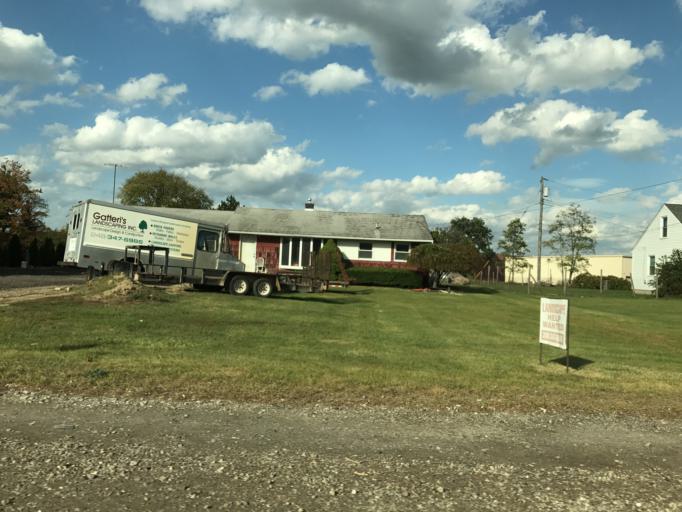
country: US
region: Michigan
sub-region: Oakland County
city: Wixom
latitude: 42.4963
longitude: -83.5451
